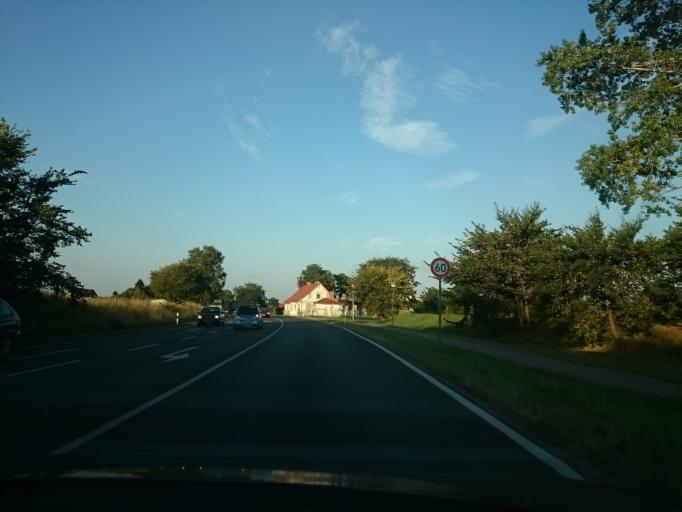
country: DE
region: Mecklenburg-Vorpommern
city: Karlshagen
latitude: 54.0702
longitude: 13.8606
